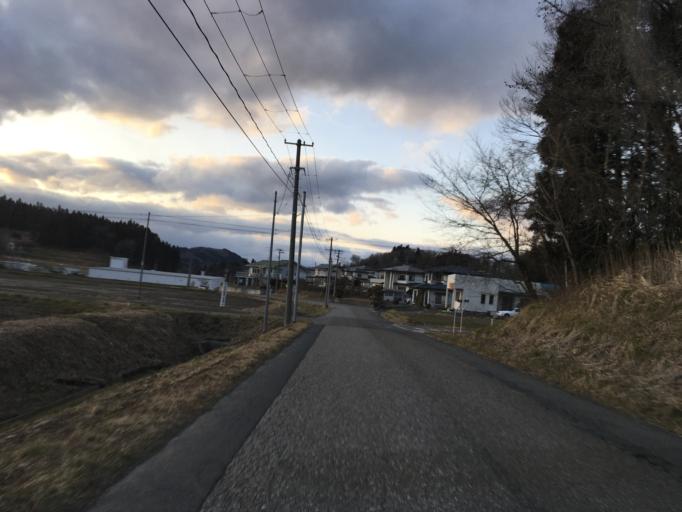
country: JP
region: Iwate
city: Ichinoseki
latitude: 38.8679
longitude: 141.3564
